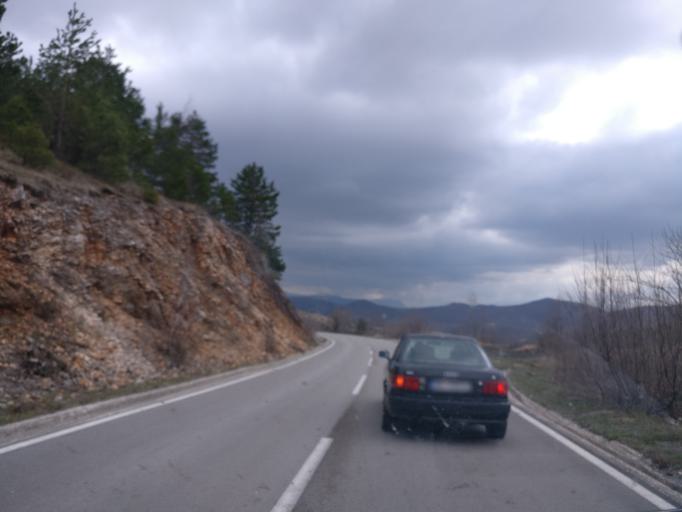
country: ME
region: Opstina Niksic
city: Niksic
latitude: 42.9356
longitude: 18.9337
